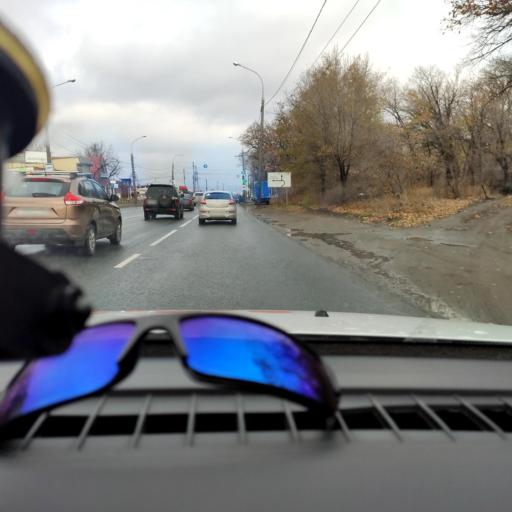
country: RU
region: Samara
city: Samara
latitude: 53.1301
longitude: 50.1721
